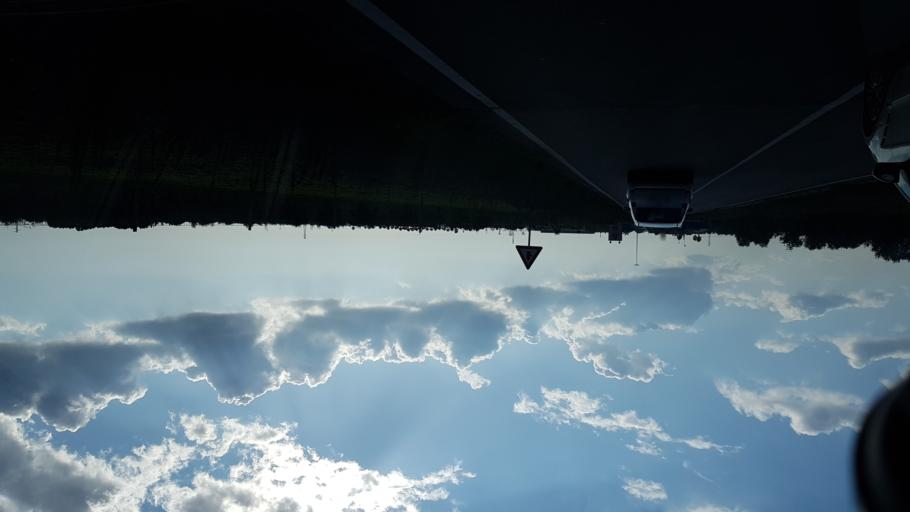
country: IT
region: Apulia
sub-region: Provincia di Lecce
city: Veglie
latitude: 40.3534
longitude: 17.9684
